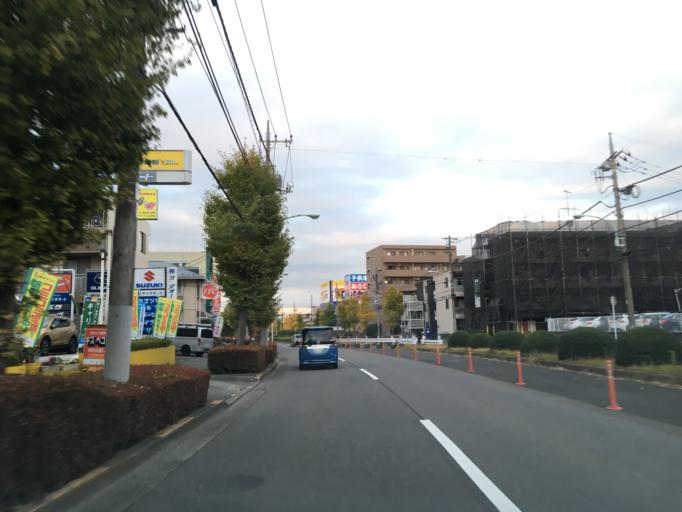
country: JP
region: Tokyo
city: Hino
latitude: 35.6200
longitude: 139.3897
